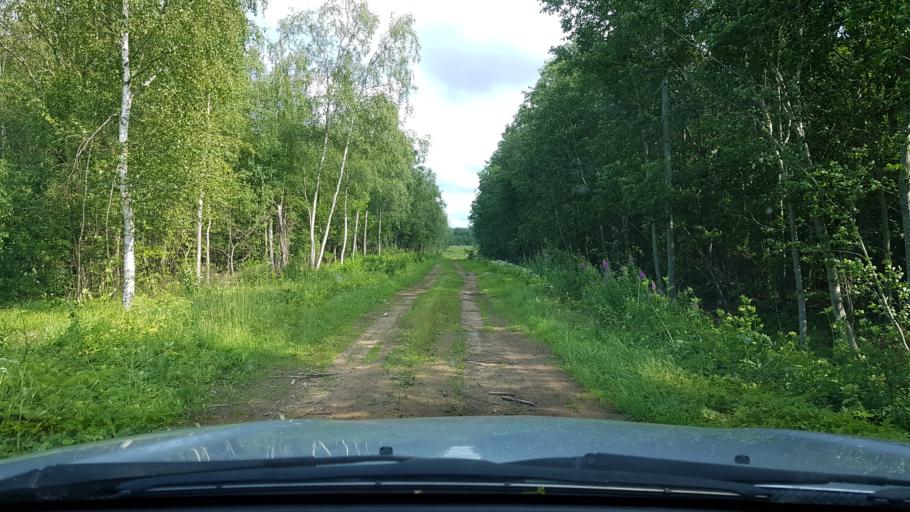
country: EE
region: Ida-Virumaa
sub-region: Narva-Joesuu linn
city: Narva-Joesuu
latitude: 59.3826
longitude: 27.9539
